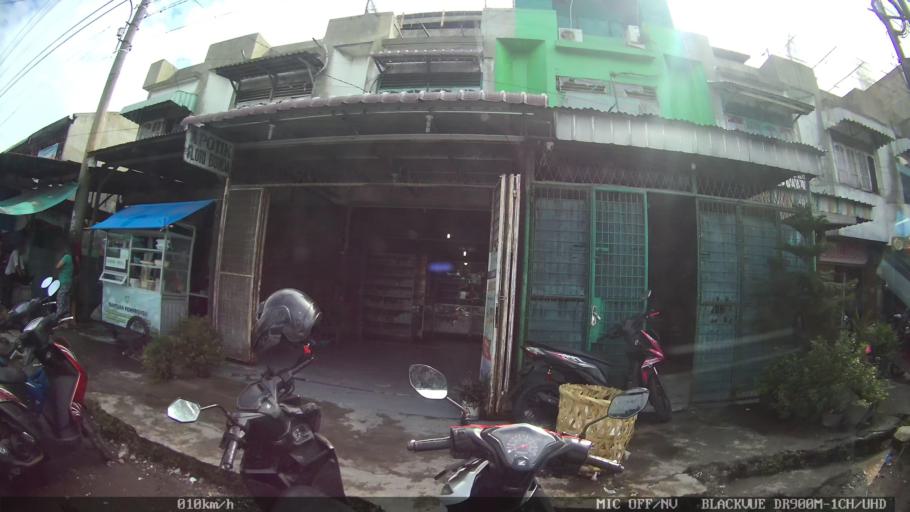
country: ID
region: North Sumatra
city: Medan
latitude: 3.6123
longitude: 98.6401
